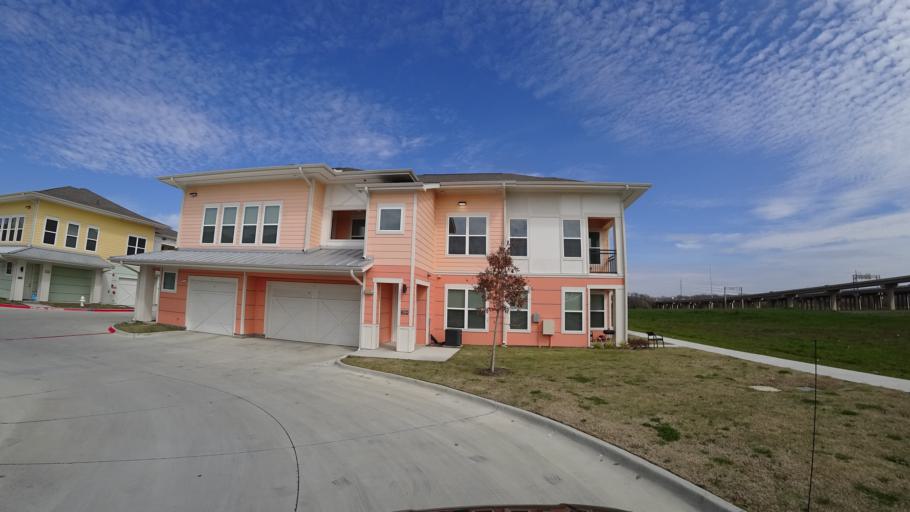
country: US
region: Texas
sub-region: Denton County
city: Lewisville
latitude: 33.0039
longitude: -96.9579
